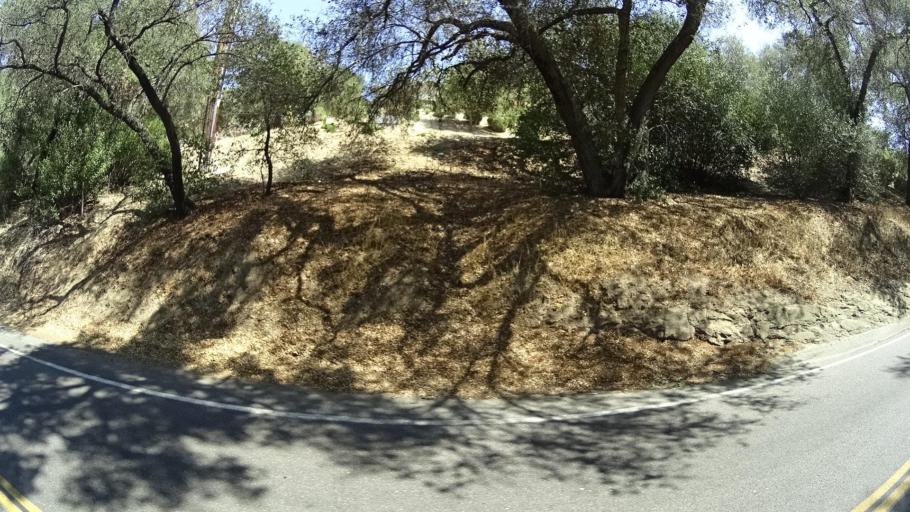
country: US
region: California
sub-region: San Diego County
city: Fallbrook
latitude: 33.3948
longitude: -117.2524
